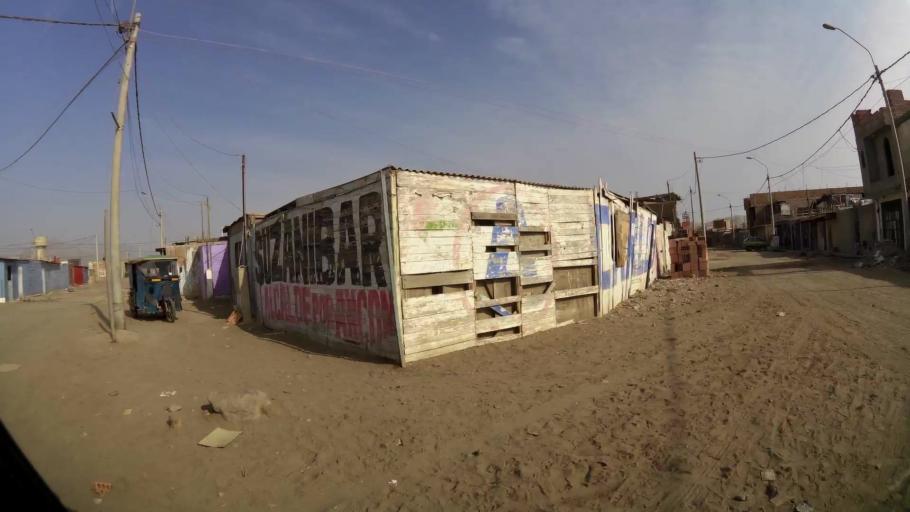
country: PE
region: Lima
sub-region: Lima
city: Santa Rosa
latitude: -11.7633
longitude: -77.1674
